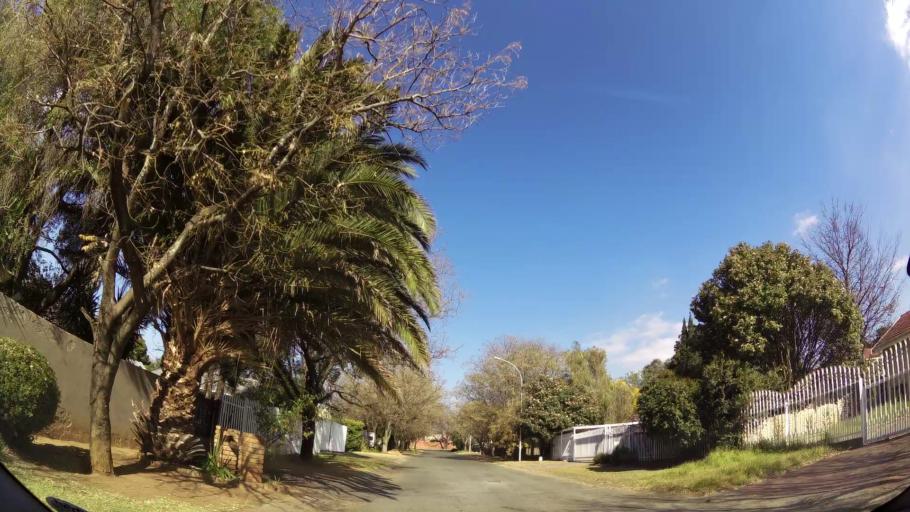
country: ZA
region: Gauteng
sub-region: Ekurhuleni Metropolitan Municipality
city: Benoni
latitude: -26.1397
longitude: 28.3509
